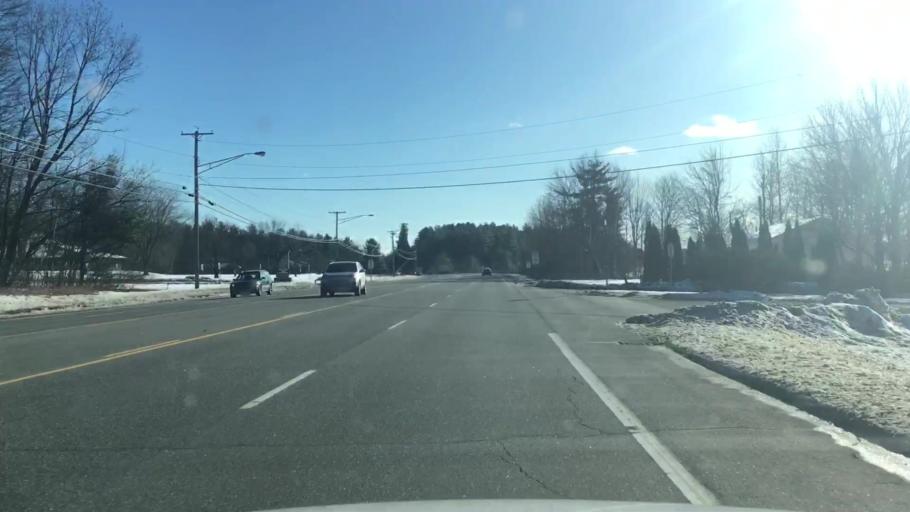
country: US
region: Maine
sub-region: Androscoggin County
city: Auburn
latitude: 44.1565
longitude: -70.2334
